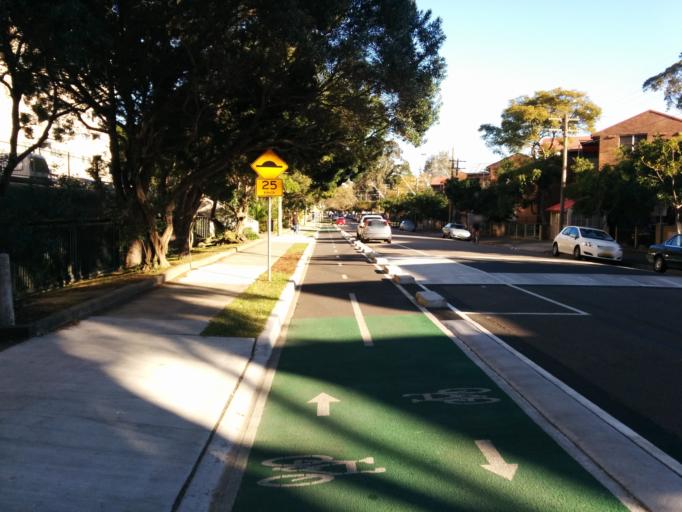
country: AU
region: New South Wales
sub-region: City of Sydney
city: Redfern
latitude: -33.8970
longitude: 151.2021
